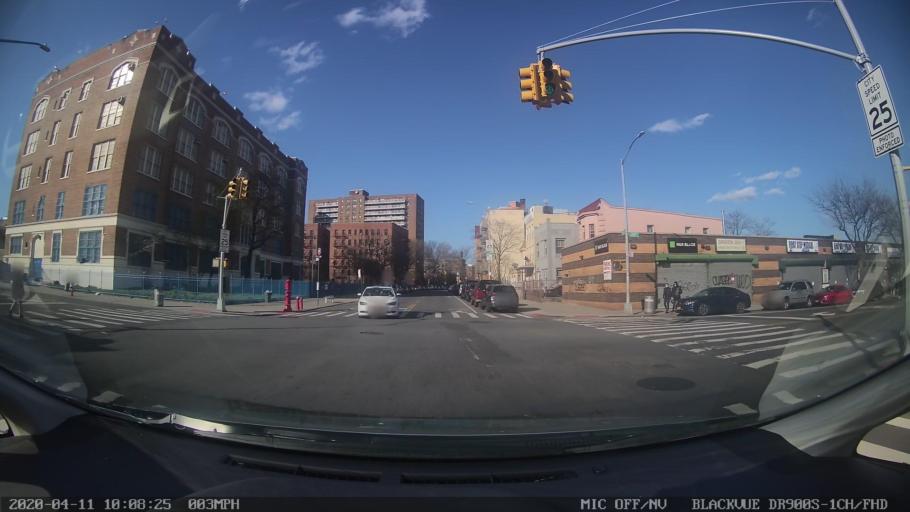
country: US
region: New York
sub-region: Bronx
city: The Bronx
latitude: 40.8481
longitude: -73.8888
